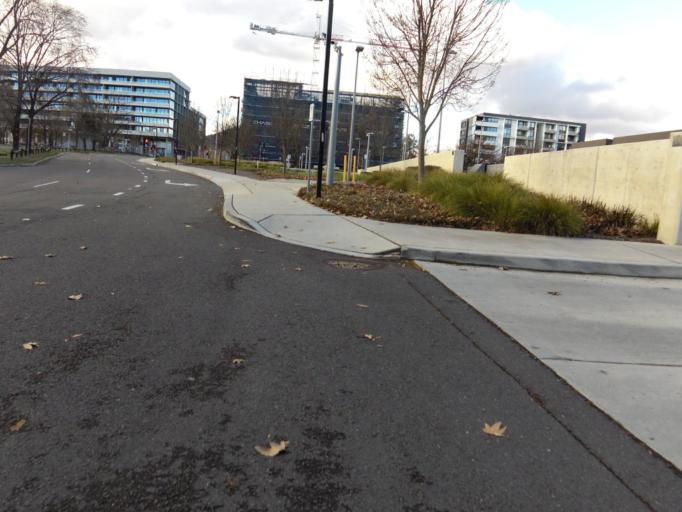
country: AU
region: Australian Capital Territory
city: Canberra
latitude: -35.2919
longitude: 149.1429
